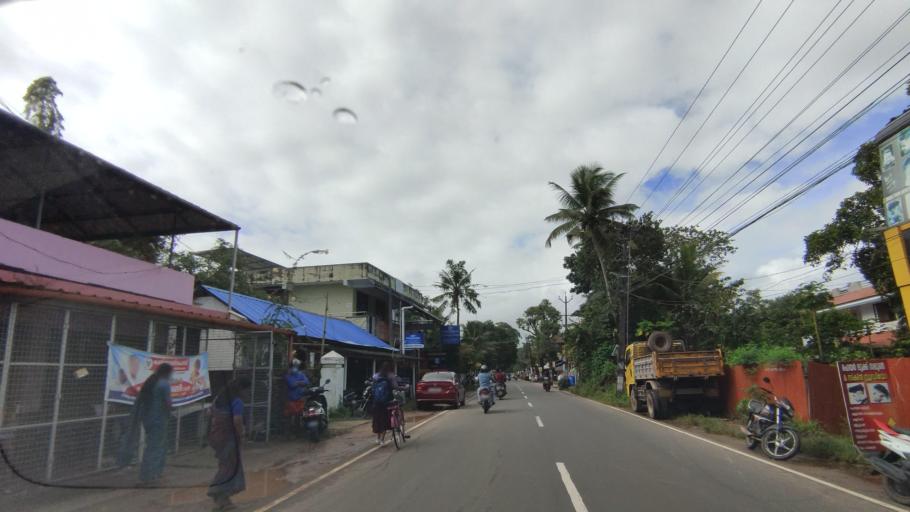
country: IN
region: Kerala
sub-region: Alappuzha
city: Alleppey
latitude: 9.5392
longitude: 76.3422
